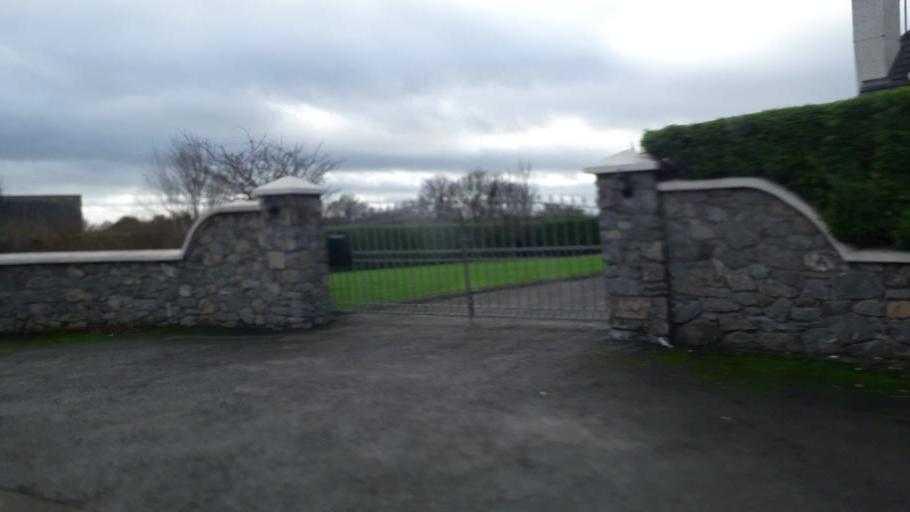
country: IE
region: Leinster
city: An Ros
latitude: 53.5428
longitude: -6.0967
